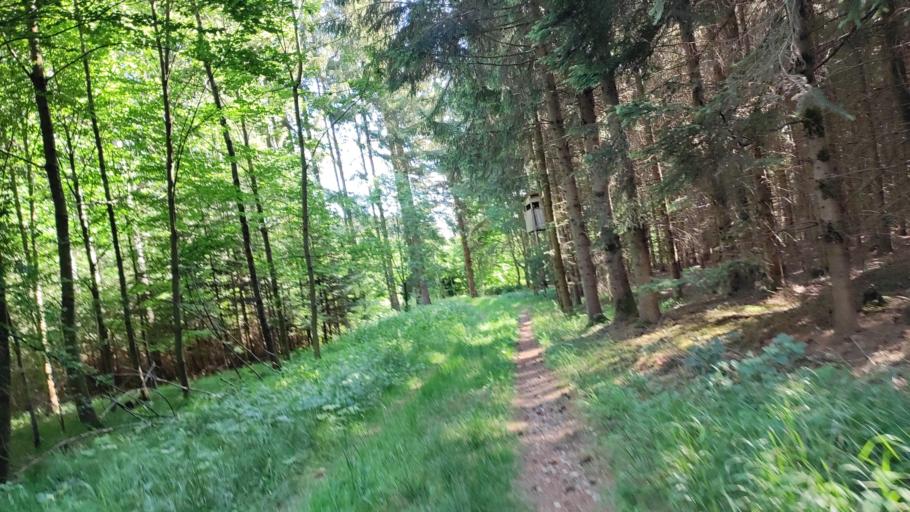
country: DE
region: Bavaria
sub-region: Swabia
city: Dinkelscherben
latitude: 48.3670
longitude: 10.6011
